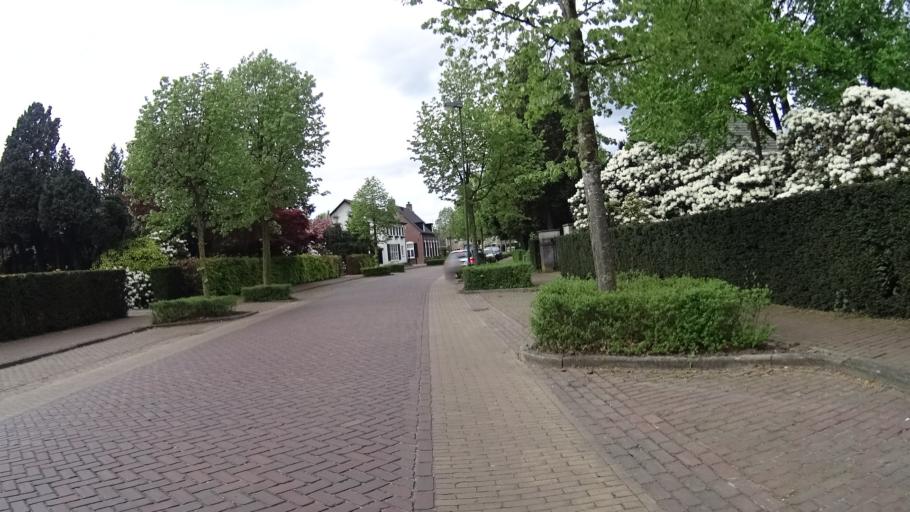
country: NL
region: North Brabant
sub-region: Gemeente Boekel
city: Boekel
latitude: 51.5494
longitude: 5.6839
